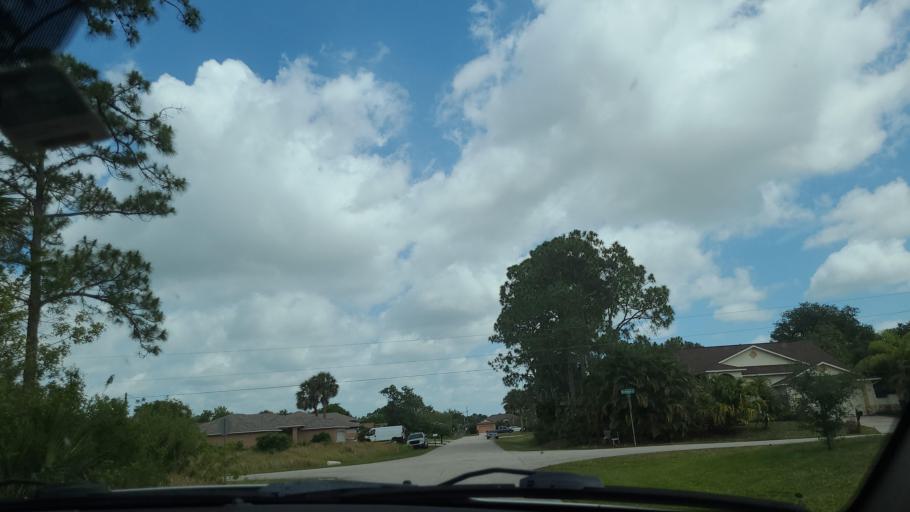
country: US
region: Florida
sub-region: Brevard County
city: West Melbourne
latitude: 28.0036
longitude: -80.6573
